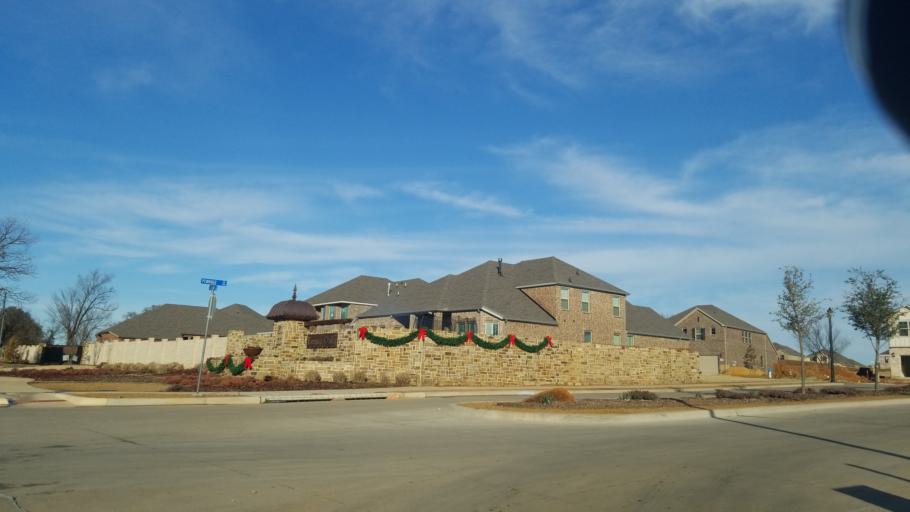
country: US
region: Texas
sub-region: Denton County
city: Corinth
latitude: 33.1461
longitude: -97.0794
